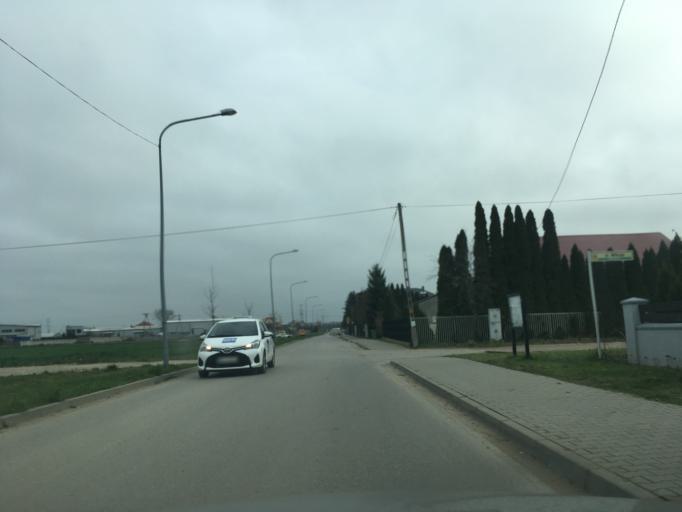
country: PL
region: Masovian Voivodeship
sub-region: Powiat piaseczynski
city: Lesznowola
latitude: 52.0825
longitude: 20.9553
